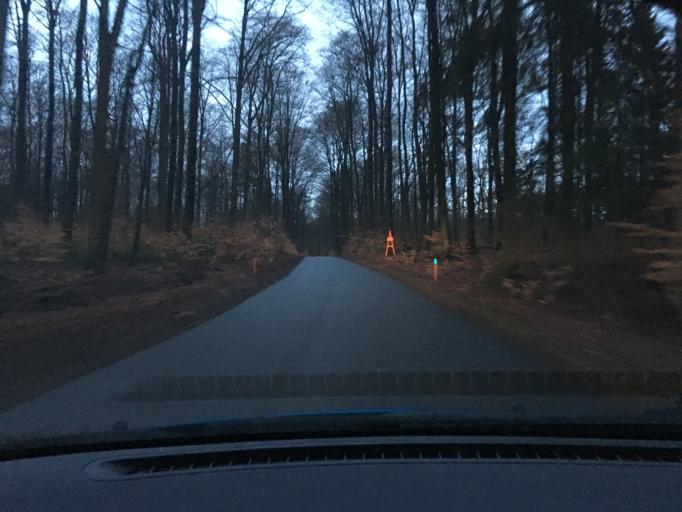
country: DE
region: Lower Saxony
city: Barnstedt
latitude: 53.1355
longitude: 10.3408
